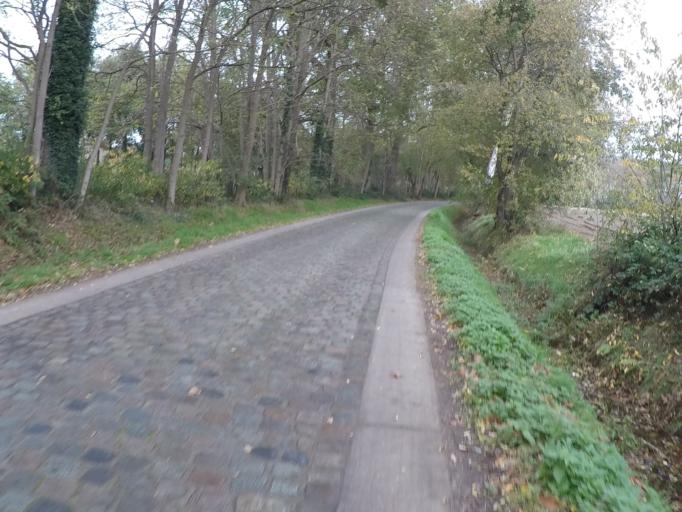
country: BE
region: Flanders
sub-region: Provincie Antwerpen
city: Berlaar
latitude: 51.1327
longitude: 4.6475
